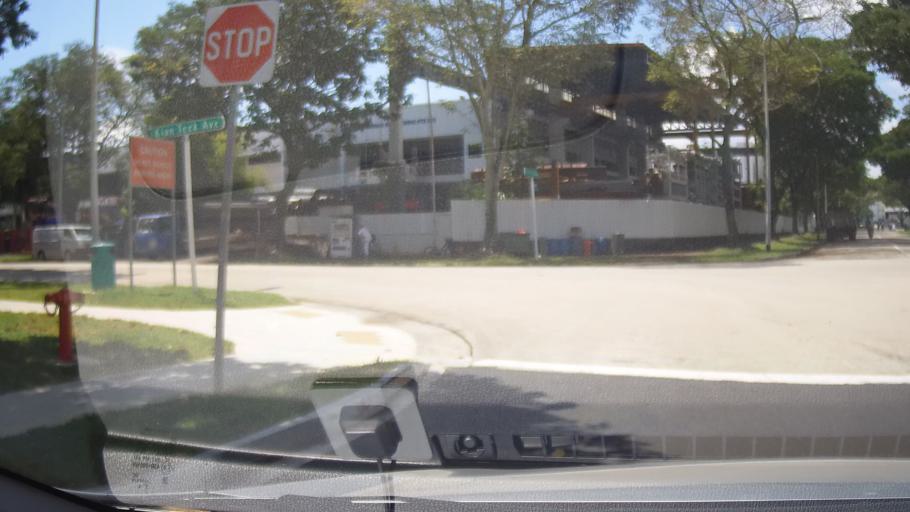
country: MY
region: Johor
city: Johor Bahru
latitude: 1.3321
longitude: 103.6938
